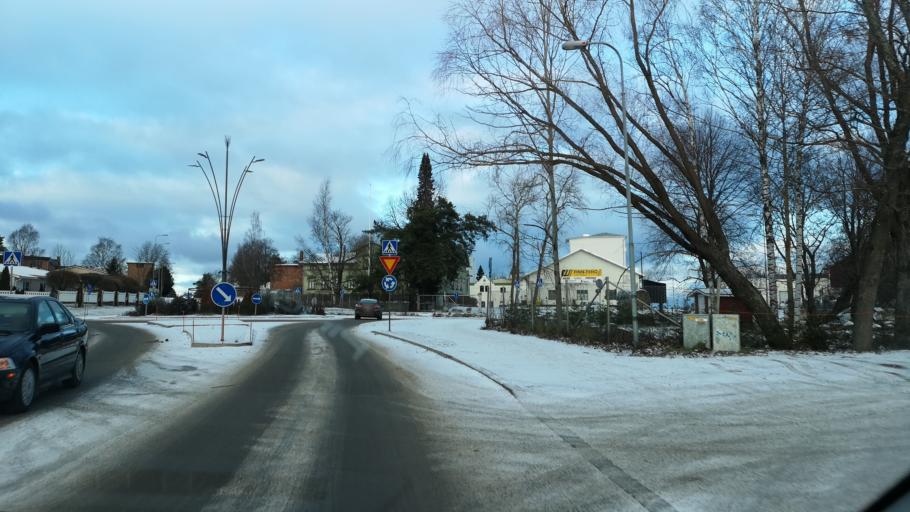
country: FI
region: Ostrobothnia
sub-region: Vaasa
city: Vaasa
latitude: 63.1156
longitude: 21.6184
